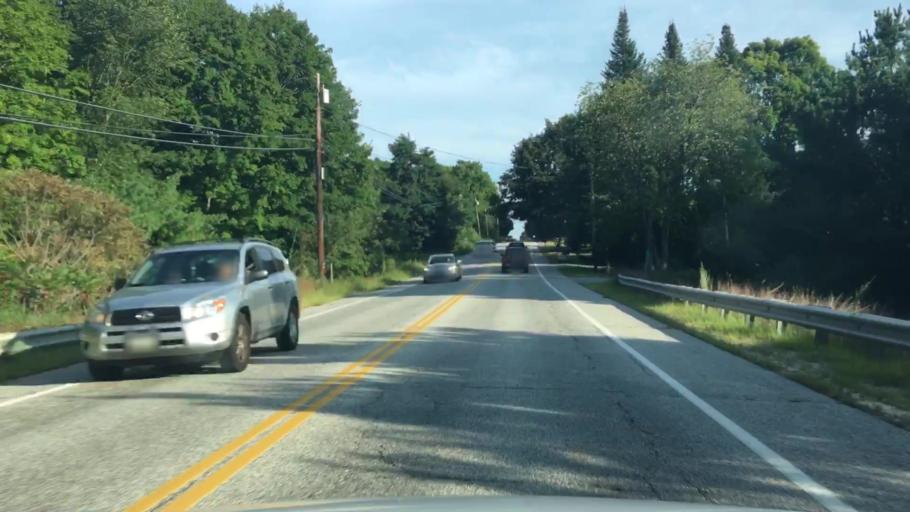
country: US
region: Maine
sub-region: Cumberland County
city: South Windham
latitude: 43.7418
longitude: -70.4218
